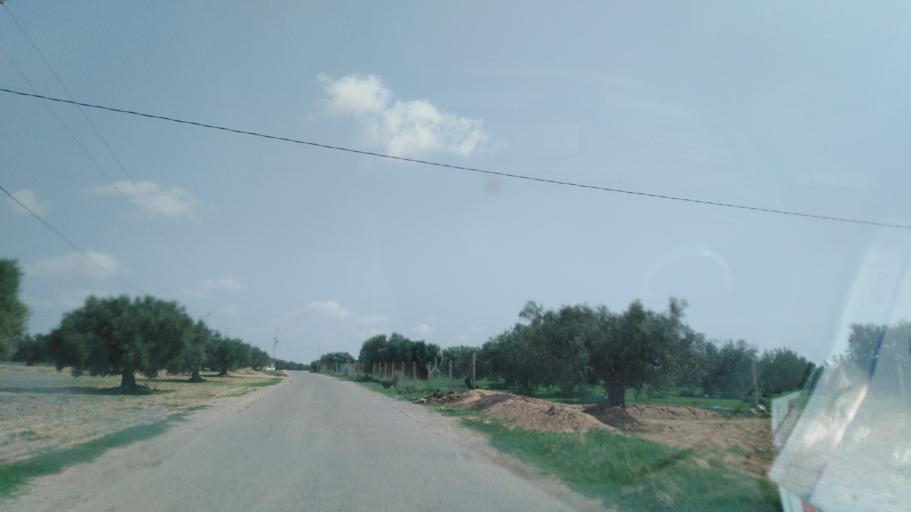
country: TN
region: Safaqis
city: Sfax
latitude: 34.6311
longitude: 10.6022
